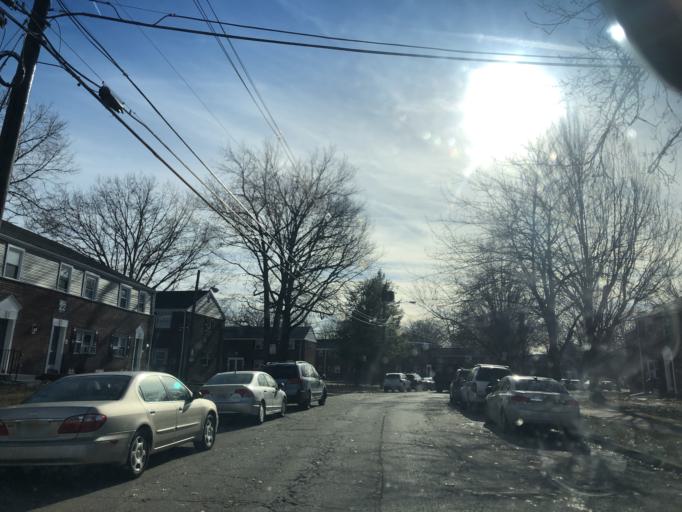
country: US
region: New Jersey
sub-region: Bergen County
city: Elmwood Park
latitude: 40.9166
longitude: -74.1257
